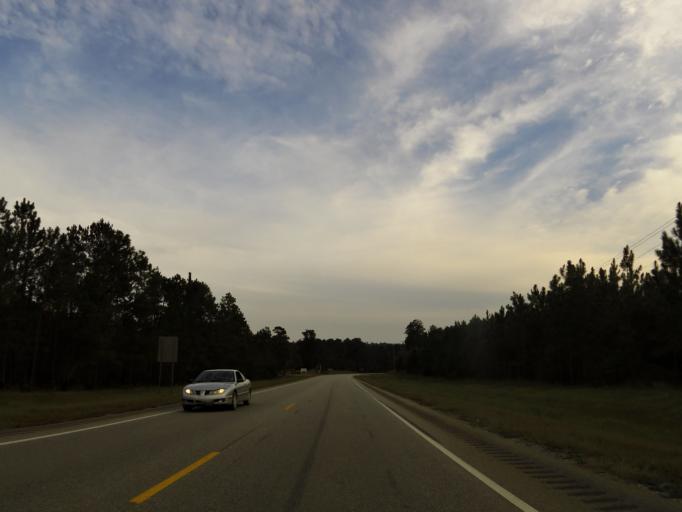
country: US
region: Alabama
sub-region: Monroe County
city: Frisco City
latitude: 31.2616
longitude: -87.4949
